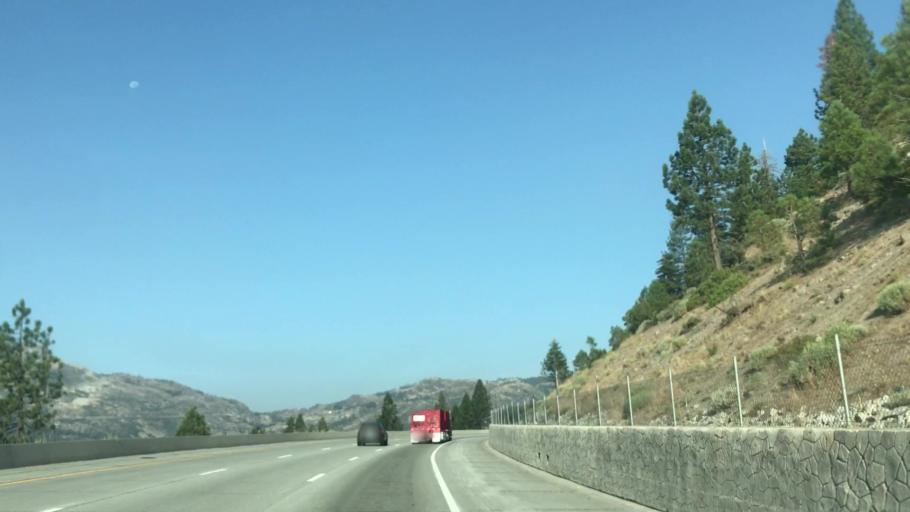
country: US
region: California
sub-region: Nevada County
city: Truckee
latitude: 39.3278
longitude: -120.2729
